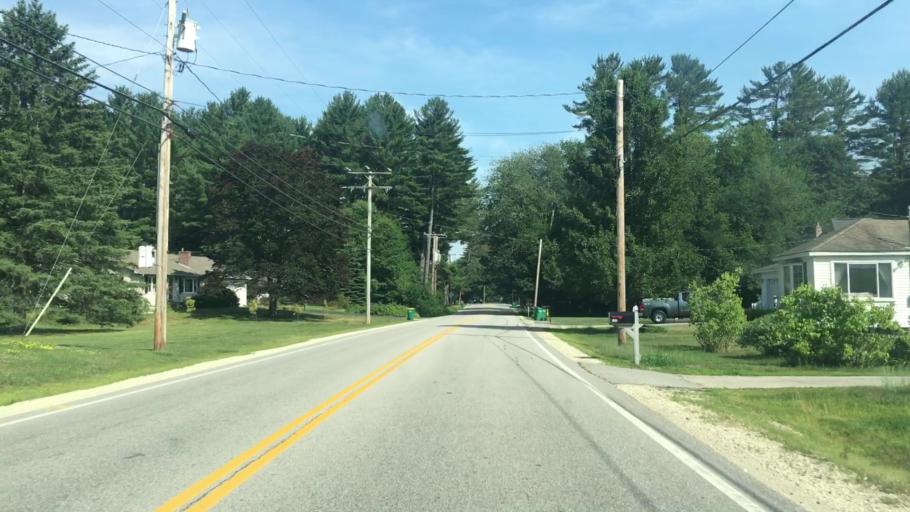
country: US
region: New Hampshire
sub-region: Strafford County
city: Rochester
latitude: 43.2720
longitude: -70.9528
